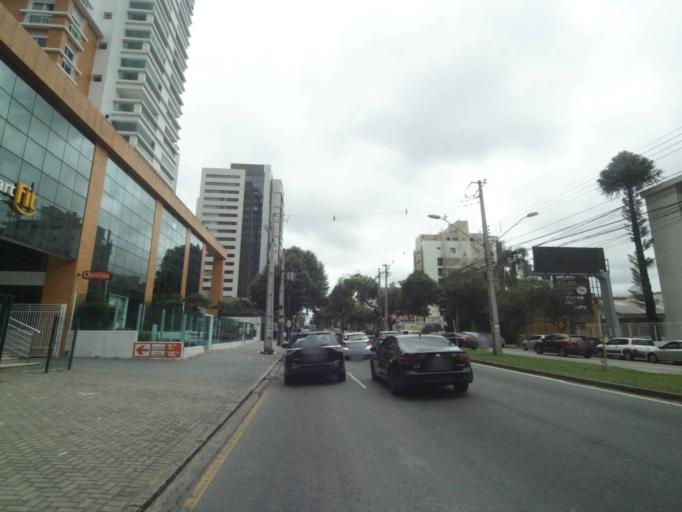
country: BR
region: Parana
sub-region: Curitiba
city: Curitiba
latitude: -25.4462
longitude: -49.2849
